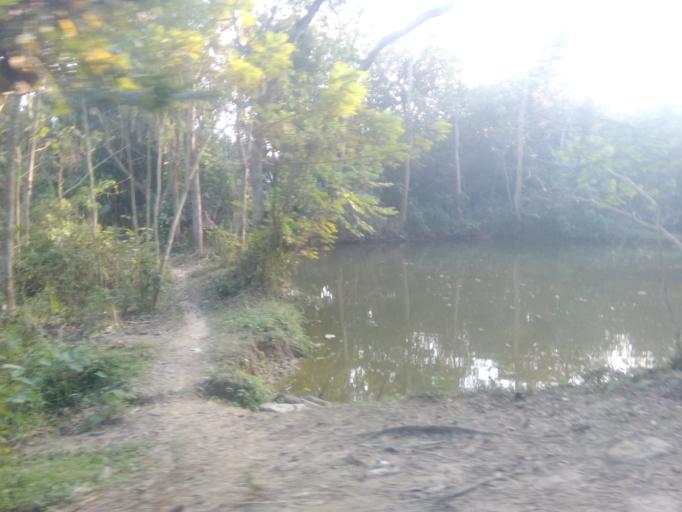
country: IN
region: Tripura
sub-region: West Tripura
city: Sonamura
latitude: 23.4139
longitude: 91.2394
